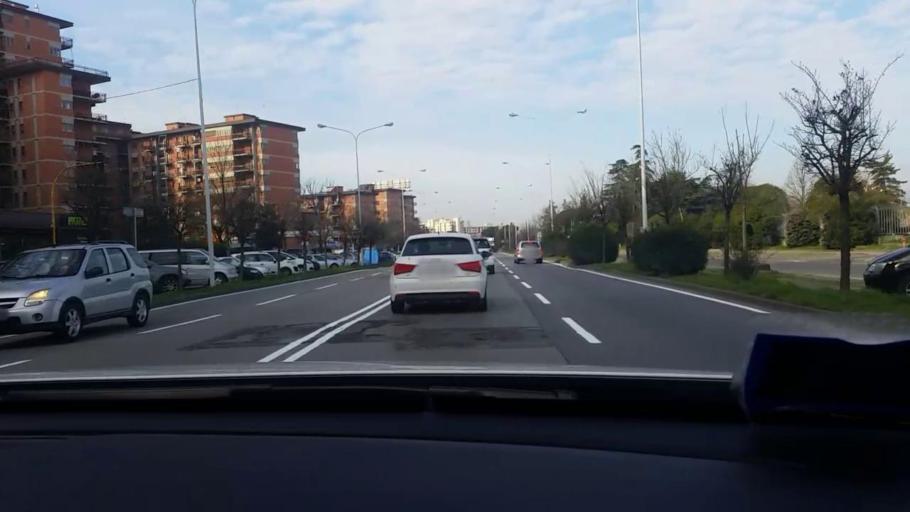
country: IT
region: Tuscany
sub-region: Province of Florence
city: Florence
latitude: 43.7980
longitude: 11.2162
